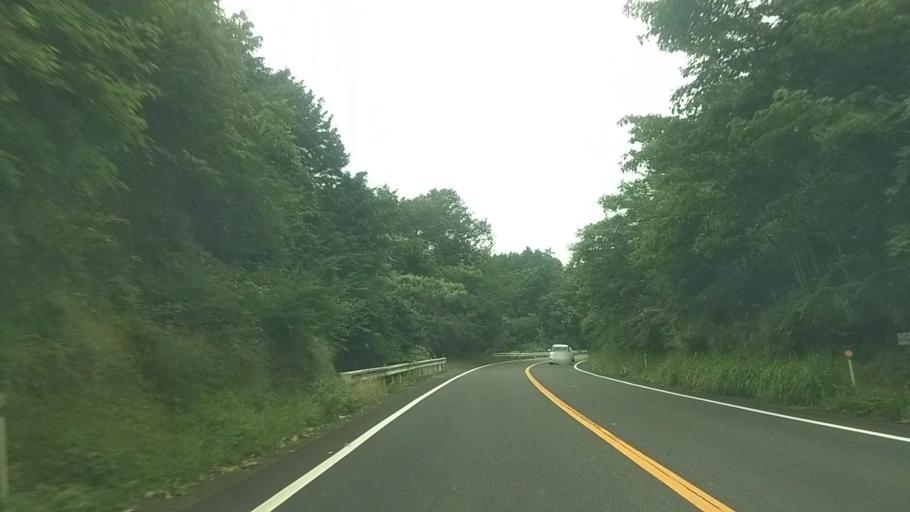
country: JP
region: Chiba
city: Kawaguchi
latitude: 35.2141
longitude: 140.0504
